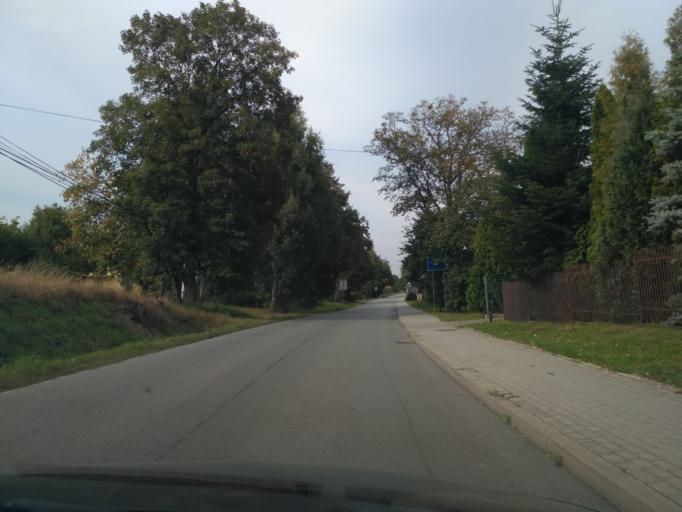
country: PL
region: Subcarpathian Voivodeship
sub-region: Powiat rzeszowski
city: Trzciana
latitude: 50.0647
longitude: 21.8351
